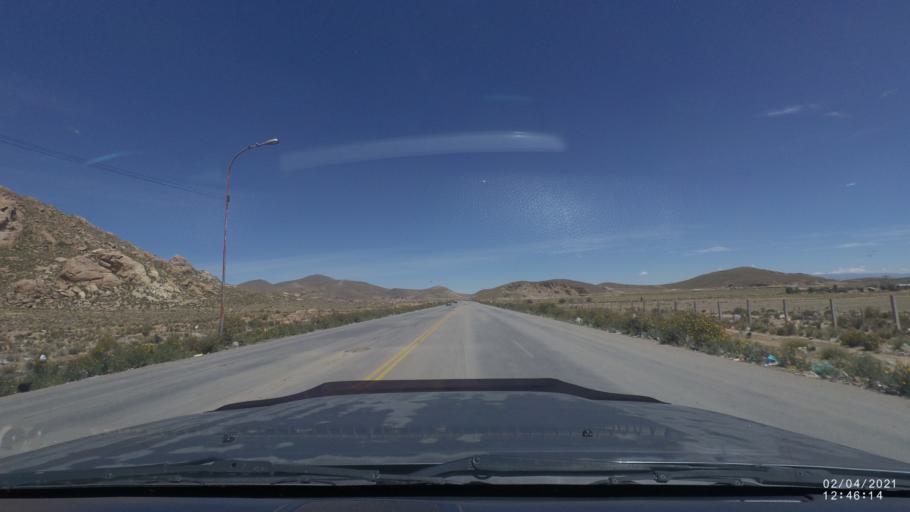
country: BO
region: Oruro
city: Oruro
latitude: -17.9429
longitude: -67.1401
